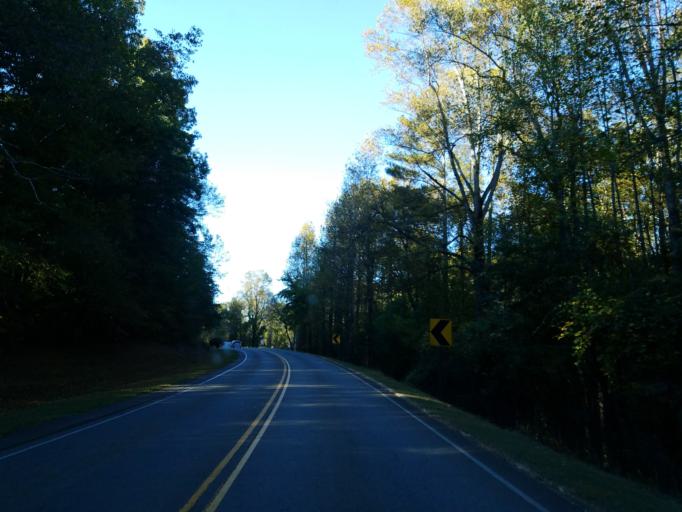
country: US
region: Georgia
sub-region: Pickens County
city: Nelson
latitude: 34.3775
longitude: -84.3717
